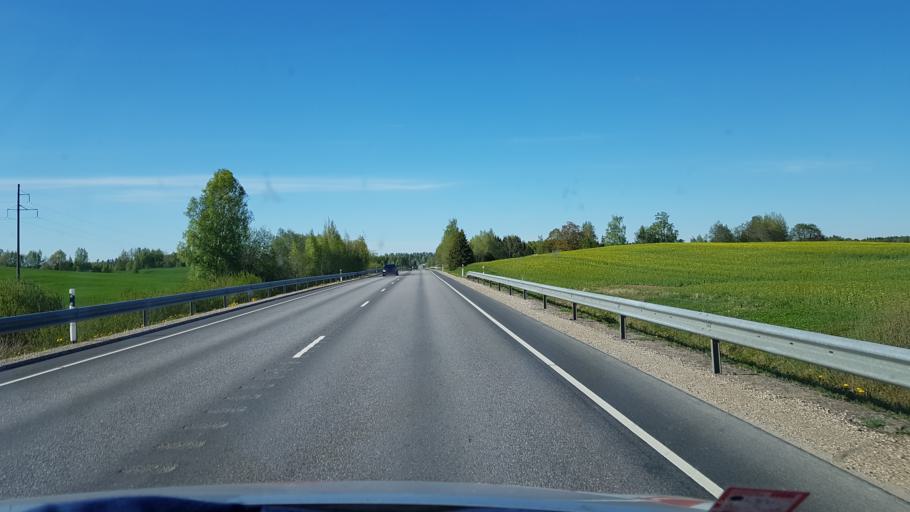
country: EE
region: Tartu
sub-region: UElenurme vald
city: Ulenurme
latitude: 58.1571
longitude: 26.6932
